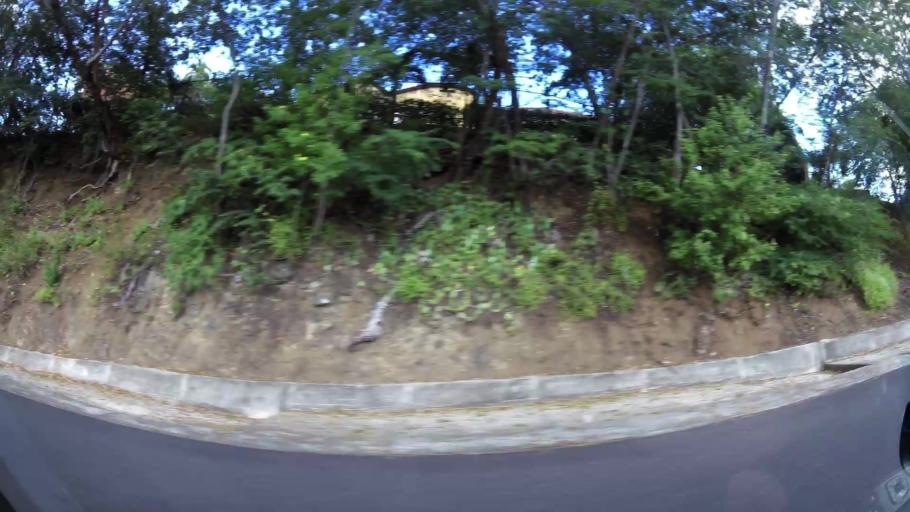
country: CR
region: Guanacaste
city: Sardinal
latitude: 10.5647
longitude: -85.6807
